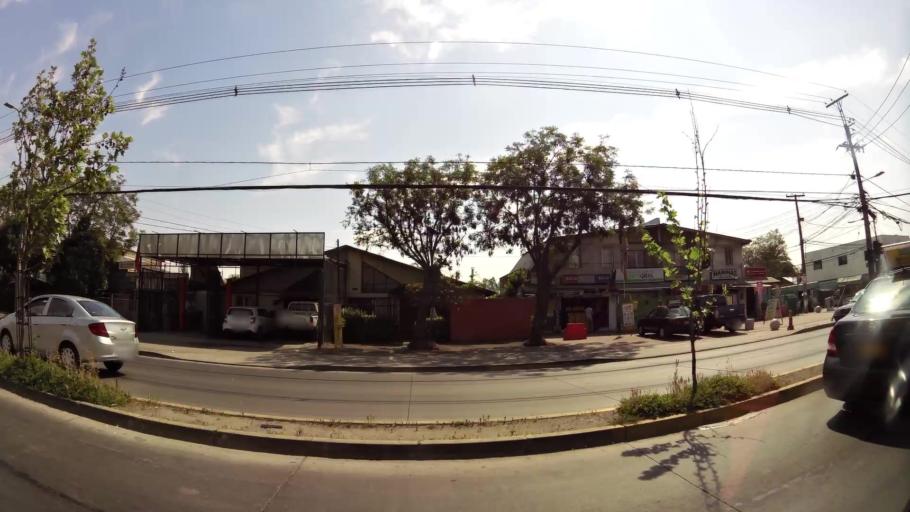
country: CL
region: Santiago Metropolitan
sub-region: Provincia de Cordillera
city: Puente Alto
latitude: -33.5801
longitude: -70.5876
